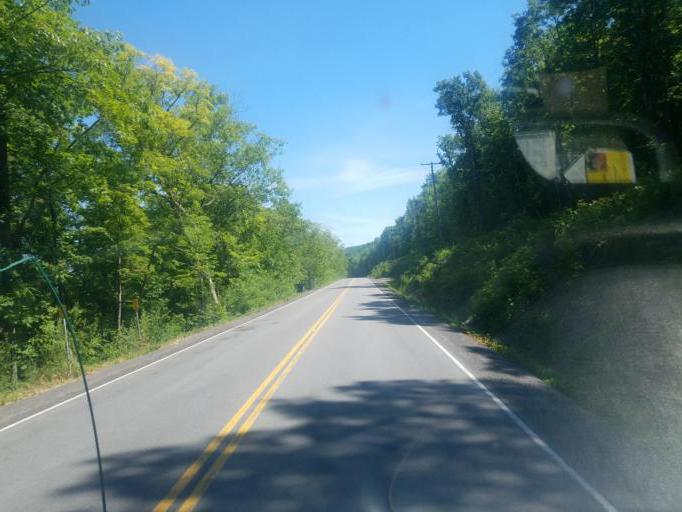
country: US
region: New York
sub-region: Ontario County
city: Canandaigua
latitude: 42.7411
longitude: -77.3187
